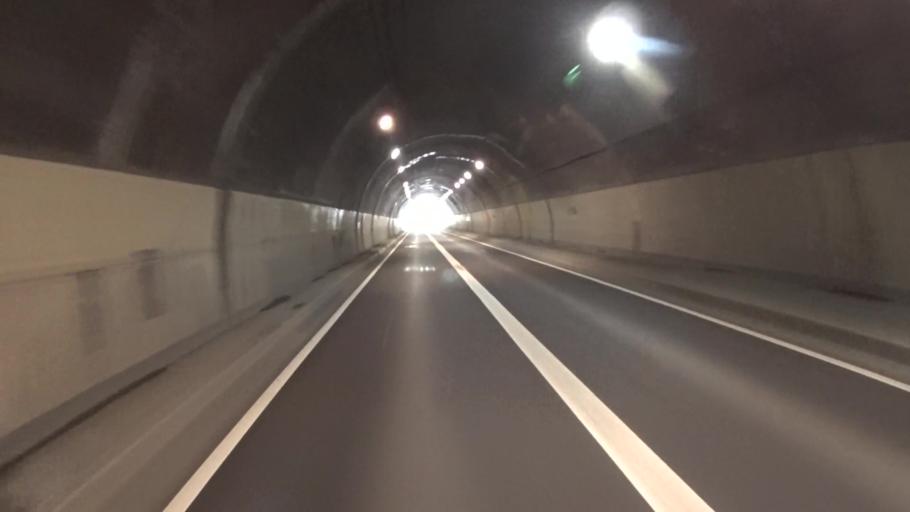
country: JP
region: Fukui
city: Obama
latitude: 35.4259
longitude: 135.9412
